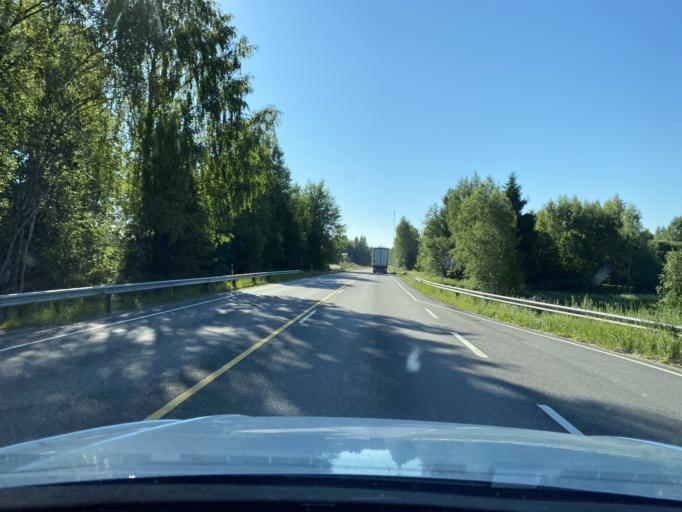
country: FI
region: Haeme
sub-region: Haemeenlinna
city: Renko
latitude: 60.7895
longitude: 24.1259
